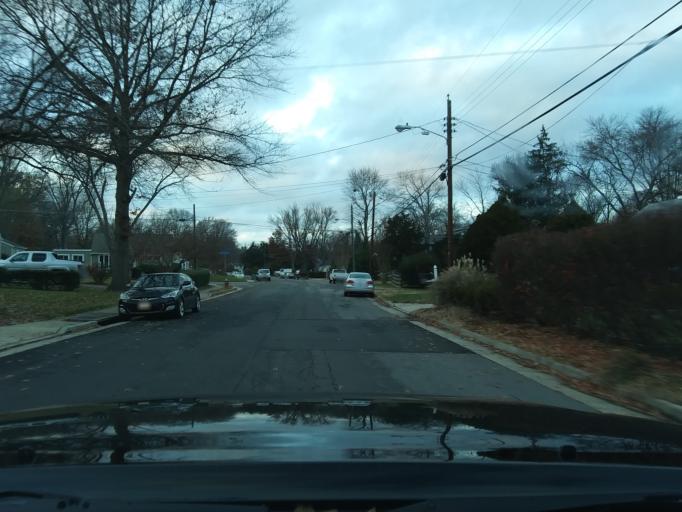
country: US
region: Virginia
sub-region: Fairfax County
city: Jefferson
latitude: 38.8651
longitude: -77.1731
